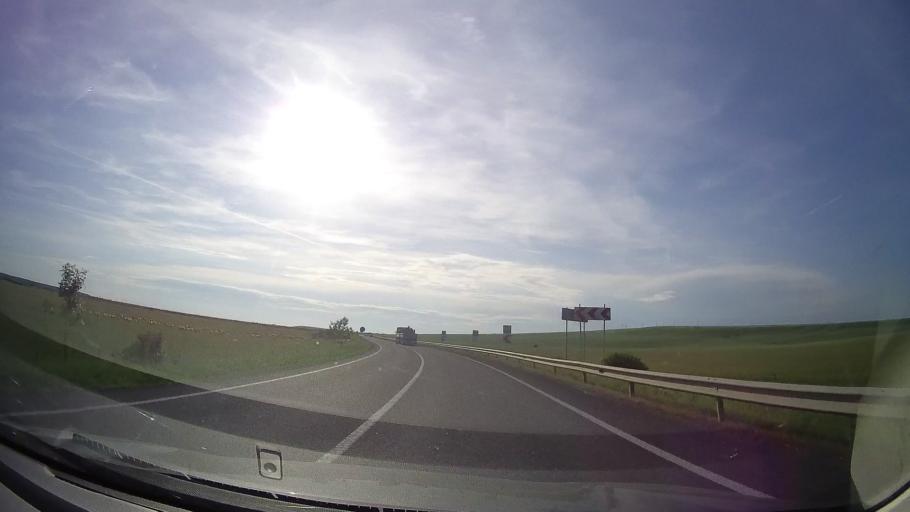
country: RO
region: Timis
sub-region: Comuna Topolovatu Mare
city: Topolovatu Mare
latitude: 45.7906
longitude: 21.5757
